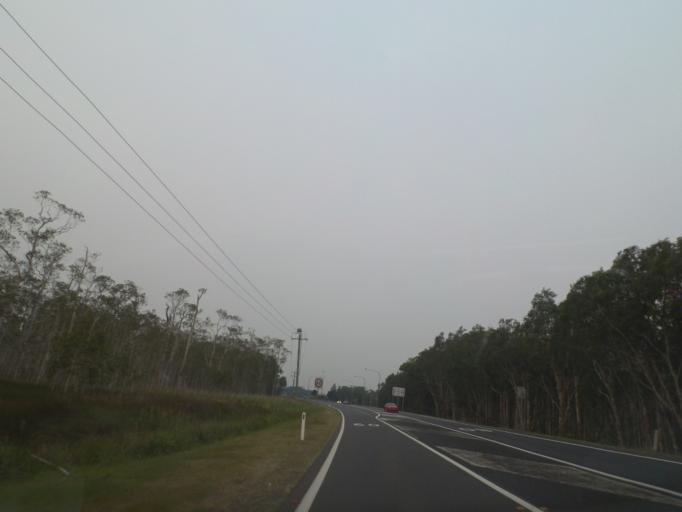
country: AU
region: New South Wales
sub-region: Coffs Harbour
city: Coffs Harbour
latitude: -30.3185
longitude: 153.1099
